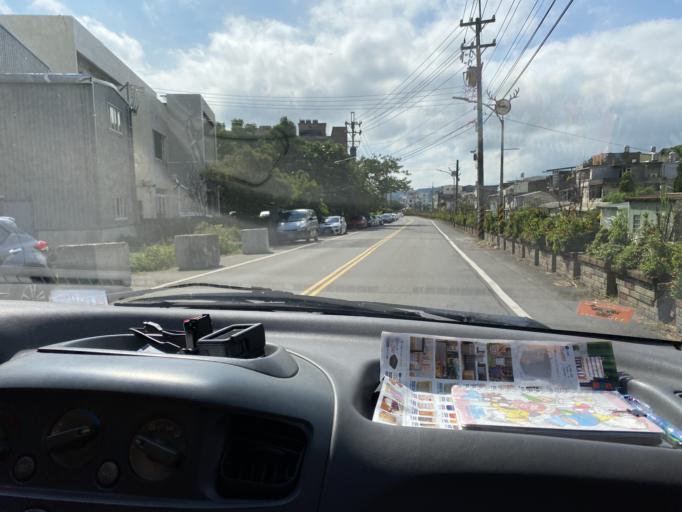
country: TW
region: Taiwan
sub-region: Hsinchu
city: Zhubei
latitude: 24.7361
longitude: 121.1230
